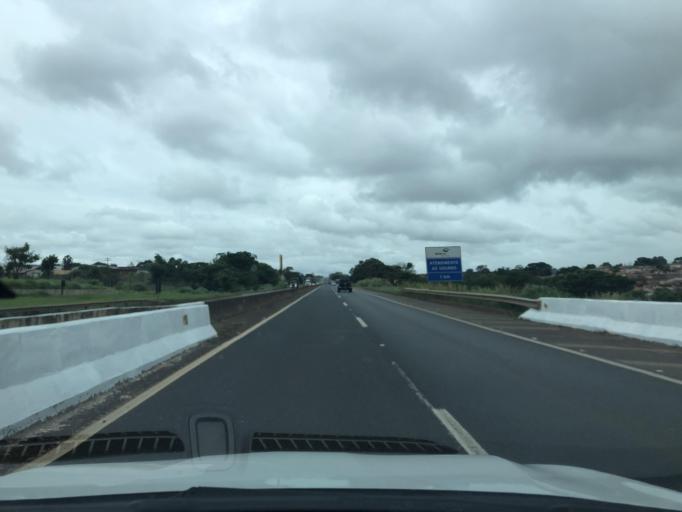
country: BR
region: Minas Gerais
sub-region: Uberaba
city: Uberaba
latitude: -19.7506
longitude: -47.9826
